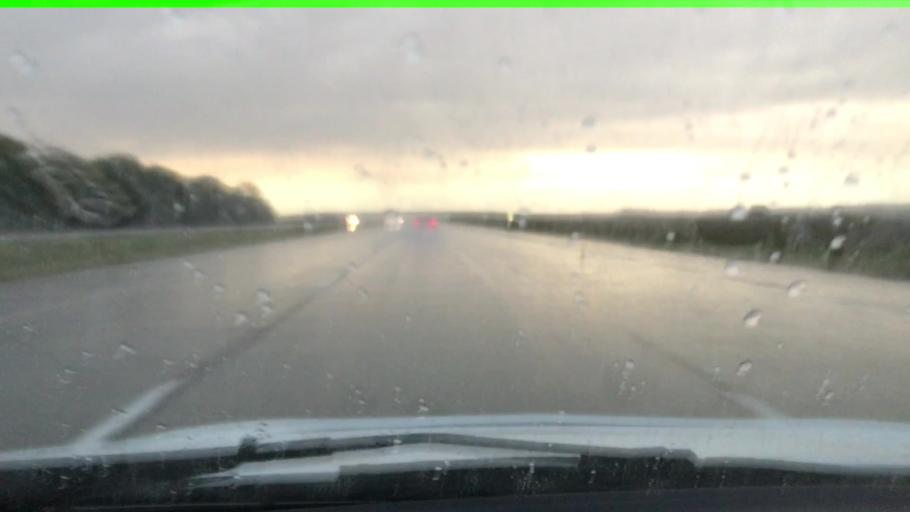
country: US
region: Nebraska
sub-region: Lancaster County
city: Waverly
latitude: 40.8968
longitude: -96.5946
